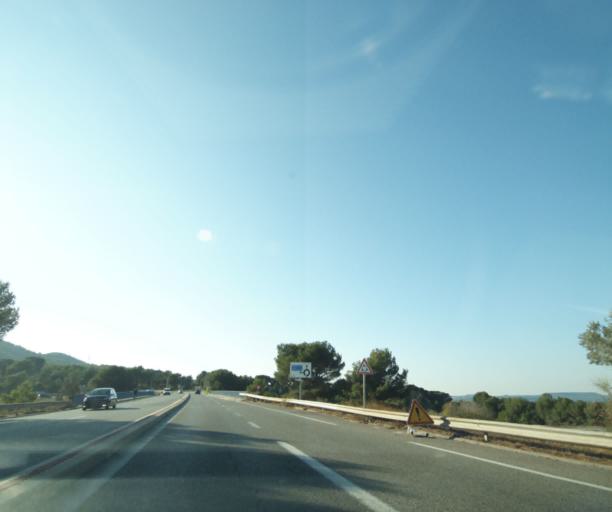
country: FR
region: Provence-Alpes-Cote d'Azur
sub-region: Departement des Bouches-du-Rhone
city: Chateauneuf-les-Martigues
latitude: 43.3947
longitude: 5.1278
